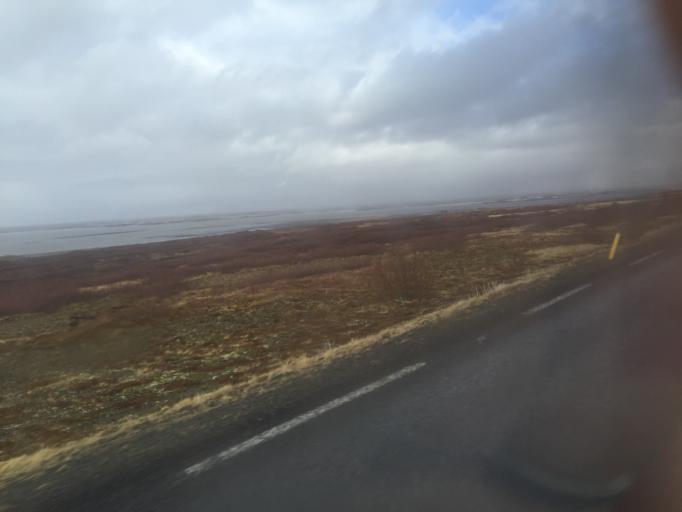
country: IS
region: West
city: Borgarnes
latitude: 64.4950
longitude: -21.9414
